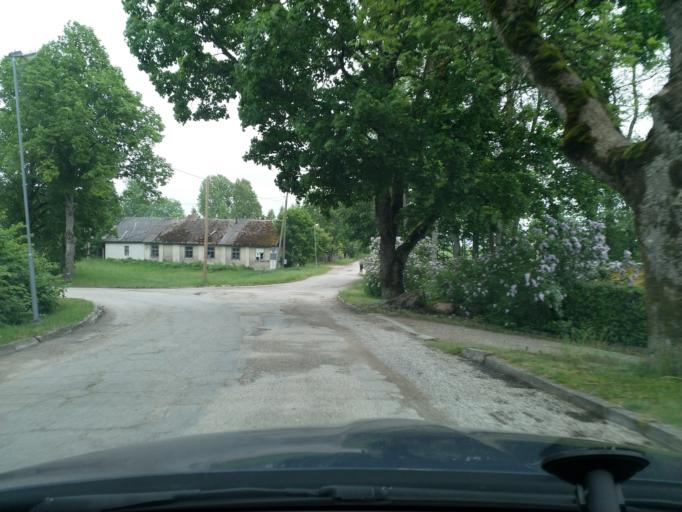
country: LV
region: Kuldigas Rajons
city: Kuldiga
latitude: 56.8811
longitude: 21.8223
